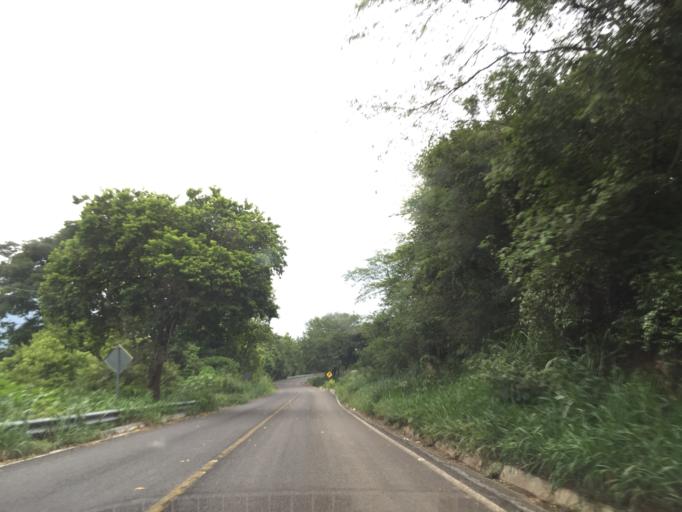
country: MX
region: Colima
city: Comala
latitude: 19.3718
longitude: -103.8030
